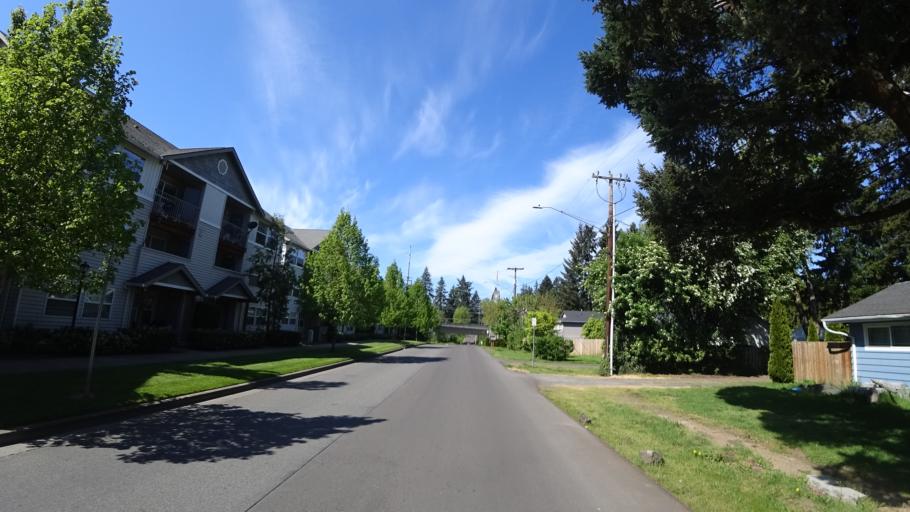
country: US
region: Oregon
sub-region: Washington County
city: Hillsboro
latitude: 45.5203
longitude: -122.9637
